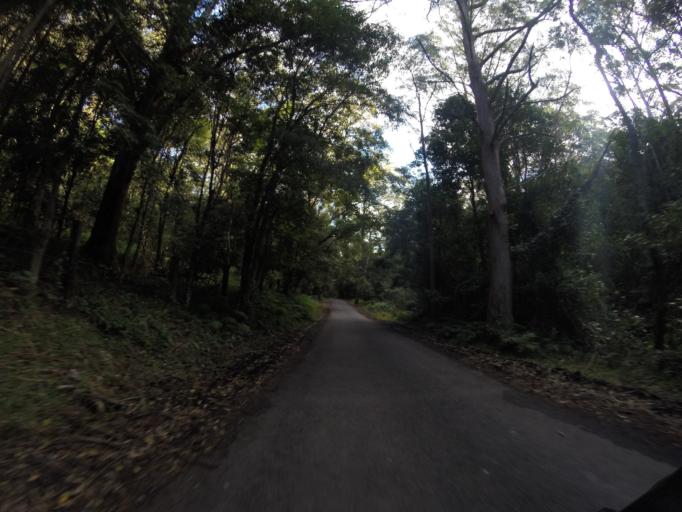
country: AU
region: New South Wales
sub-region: Wollongong
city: Cordeaux Heights
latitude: -34.4372
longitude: 150.7966
